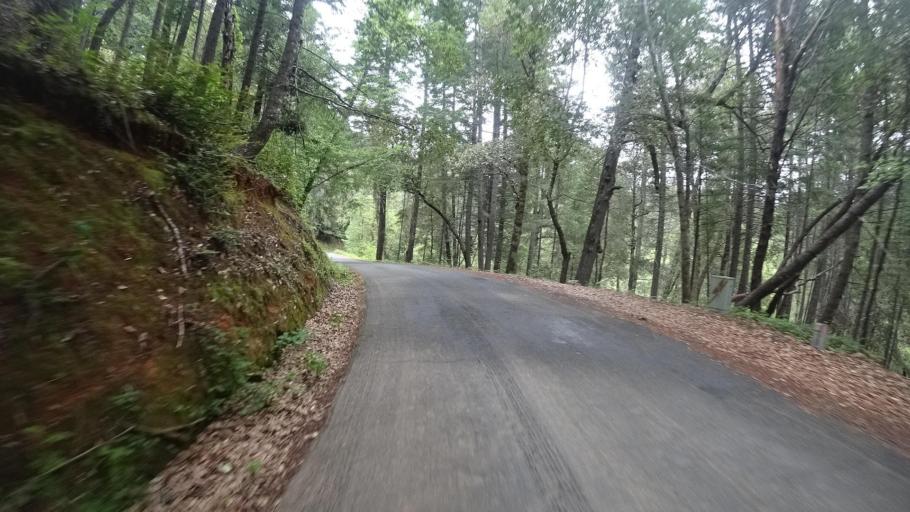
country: US
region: California
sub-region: Siskiyou County
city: Happy Camp
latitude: 41.3702
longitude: -123.5028
